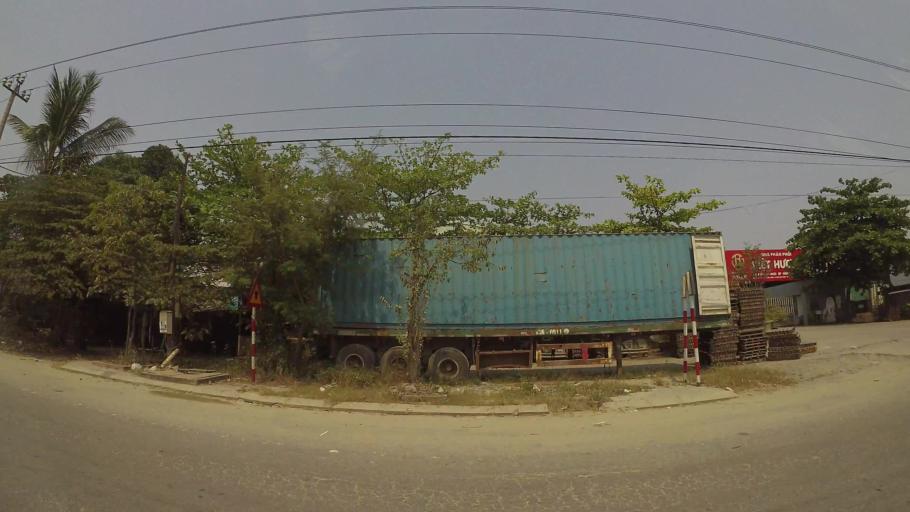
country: VN
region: Da Nang
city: Cam Le
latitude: 15.9858
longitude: 108.2020
